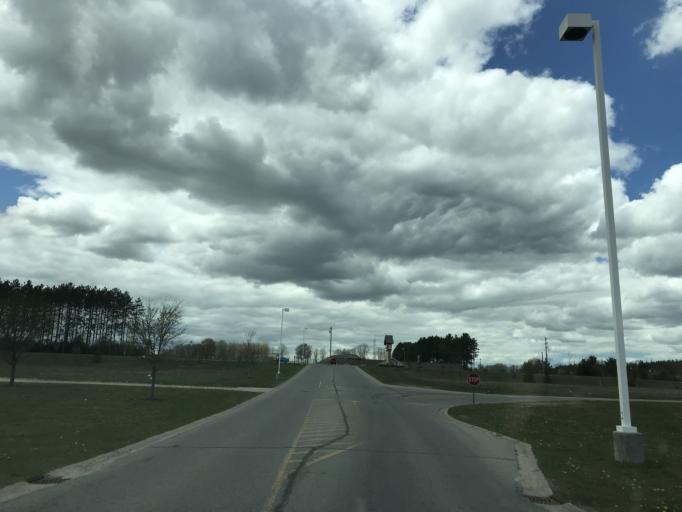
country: US
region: Michigan
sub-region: Otsego County
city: Gaylord
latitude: 45.0251
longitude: -84.7249
